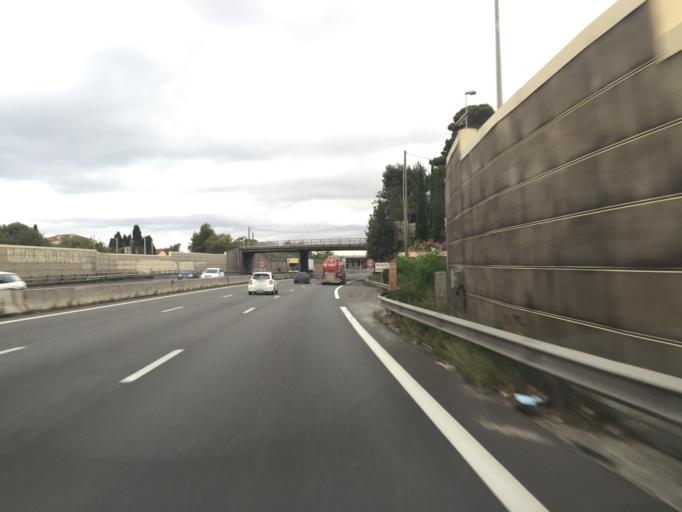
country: FR
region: Provence-Alpes-Cote d'Azur
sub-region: Departement des Alpes-Maritimes
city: Cagnes-sur-Mer
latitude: 43.6554
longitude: 7.1464
